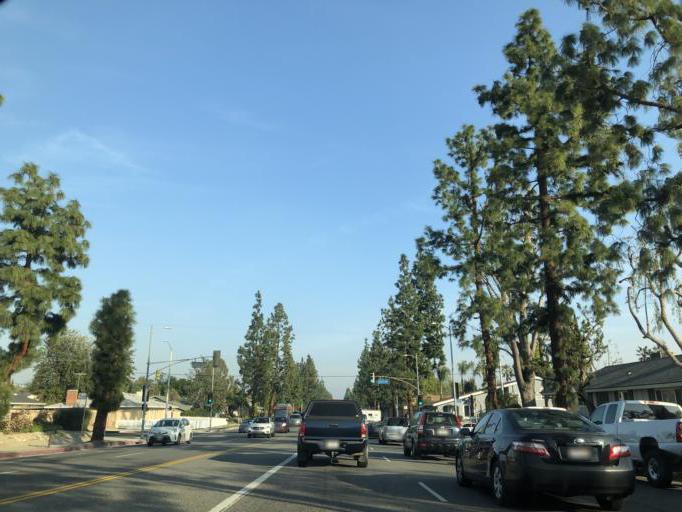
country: US
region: California
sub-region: Los Angeles County
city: Chatsworth
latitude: 34.2572
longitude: -118.5850
